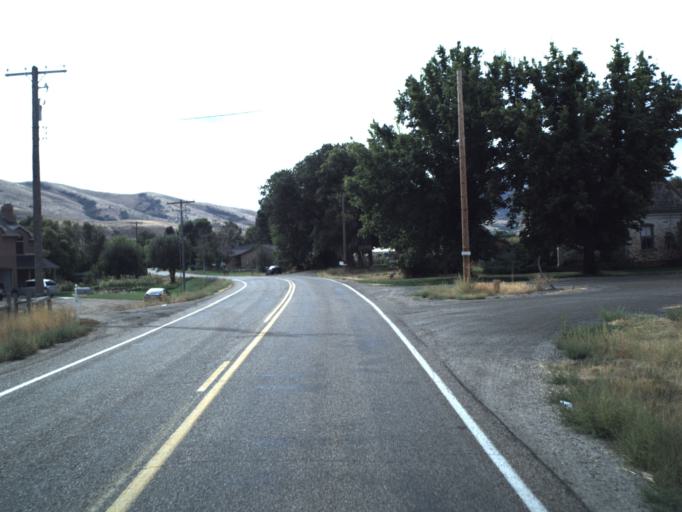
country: US
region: Utah
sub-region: Morgan County
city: Morgan
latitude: 40.9795
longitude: -111.6769
